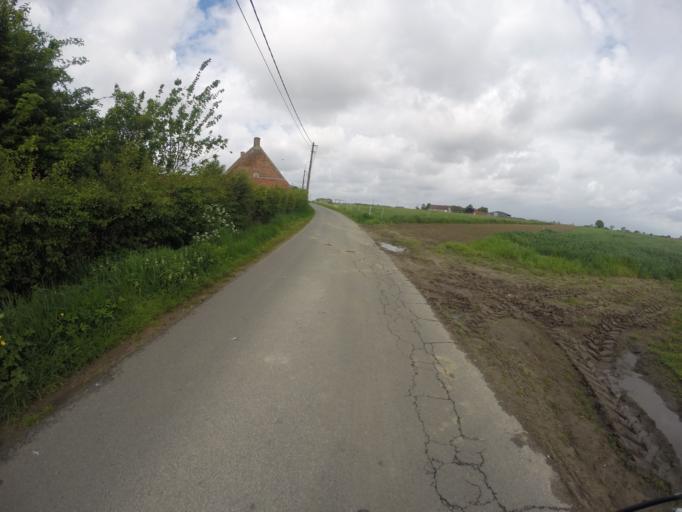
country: BE
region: Flanders
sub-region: Provincie Oost-Vlaanderen
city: Aalter
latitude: 51.0515
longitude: 3.4471
